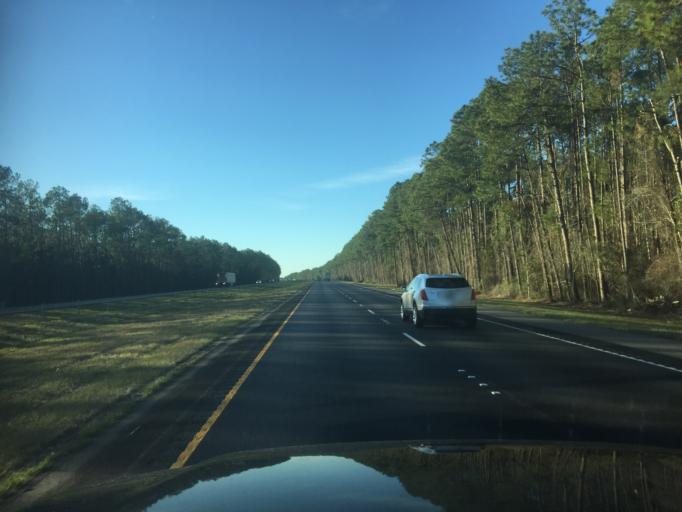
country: US
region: Louisiana
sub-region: Saint Tammany Parish
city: Lacombe
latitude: 30.3735
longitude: -89.9606
